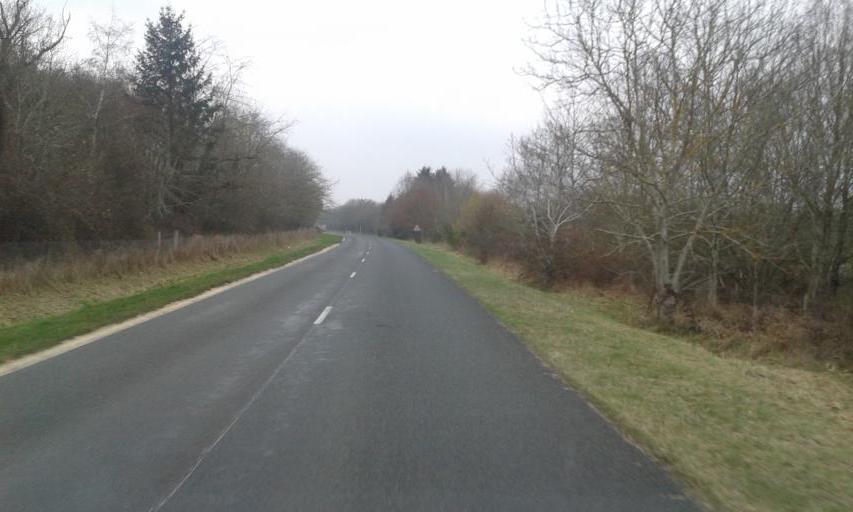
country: FR
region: Centre
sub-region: Departement du Loiret
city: Tavers
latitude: 47.7289
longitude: 1.6537
